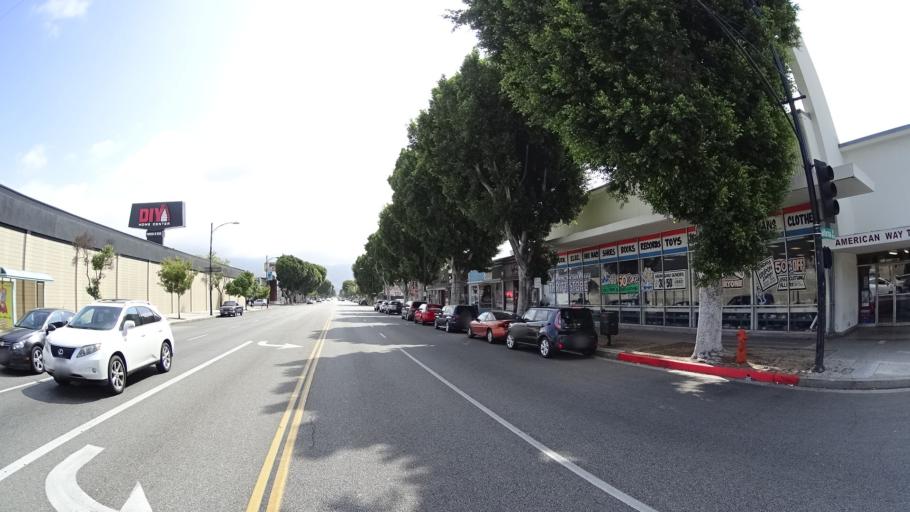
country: US
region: California
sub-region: Los Angeles County
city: Universal City
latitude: 34.1692
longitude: -118.3428
